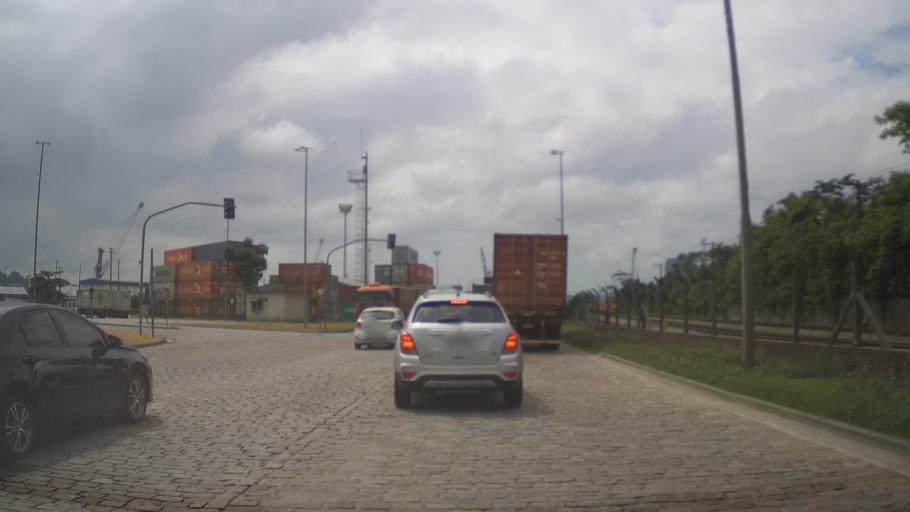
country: BR
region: Sao Paulo
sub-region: Santos
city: Santos
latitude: -23.9268
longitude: -46.3469
